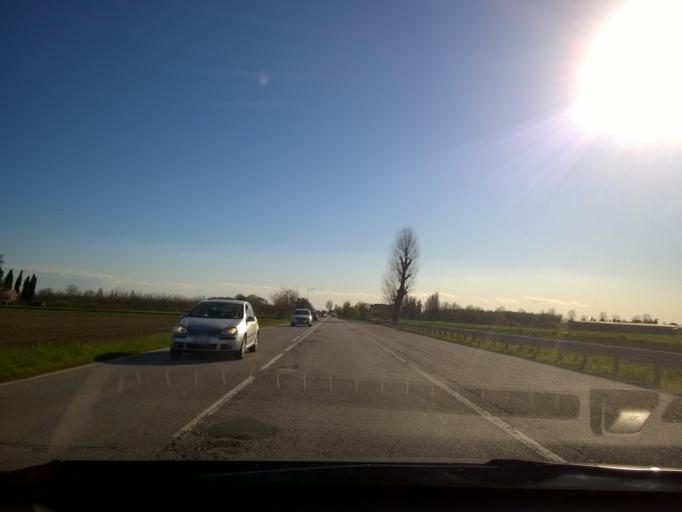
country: IT
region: Veneto
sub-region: Provincia di Venezia
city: Meolo
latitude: 45.5973
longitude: 12.4791
